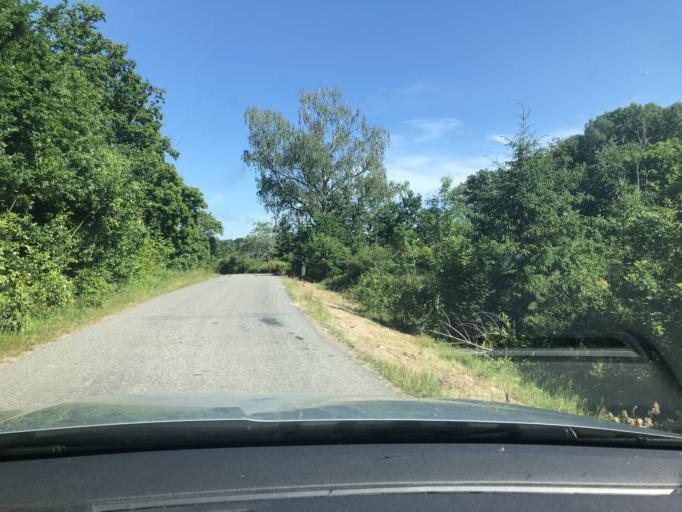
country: SE
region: Blekinge
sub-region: Karlshamns Kommun
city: Morrum
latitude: 56.1732
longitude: 14.7221
